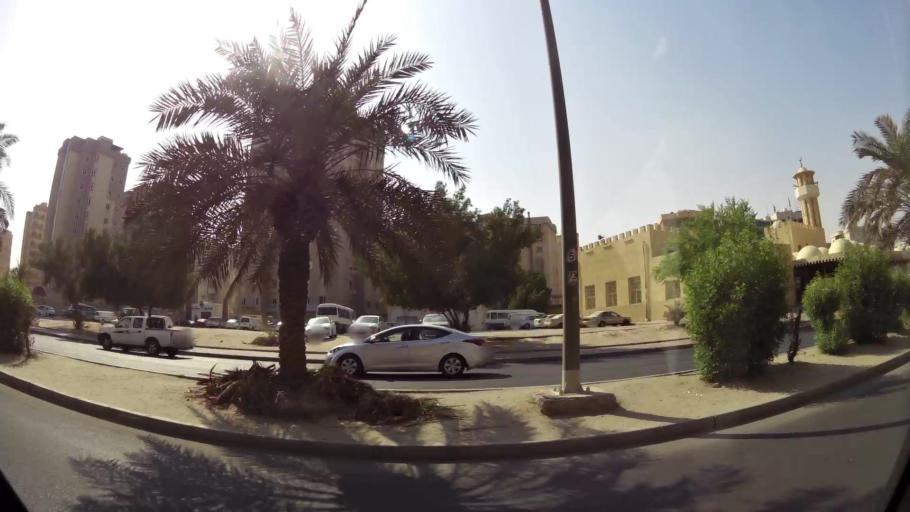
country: KW
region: Al Ahmadi
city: Al Manqaf
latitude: 29.0957
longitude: 48.1294
